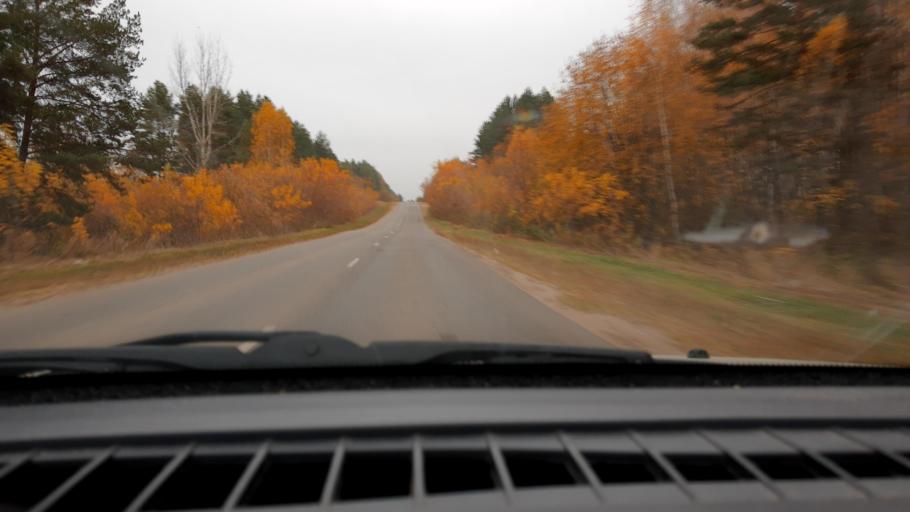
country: RU
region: Nizjnij Novgorod
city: Burevestnik
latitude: 56.0681
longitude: 43.8926
